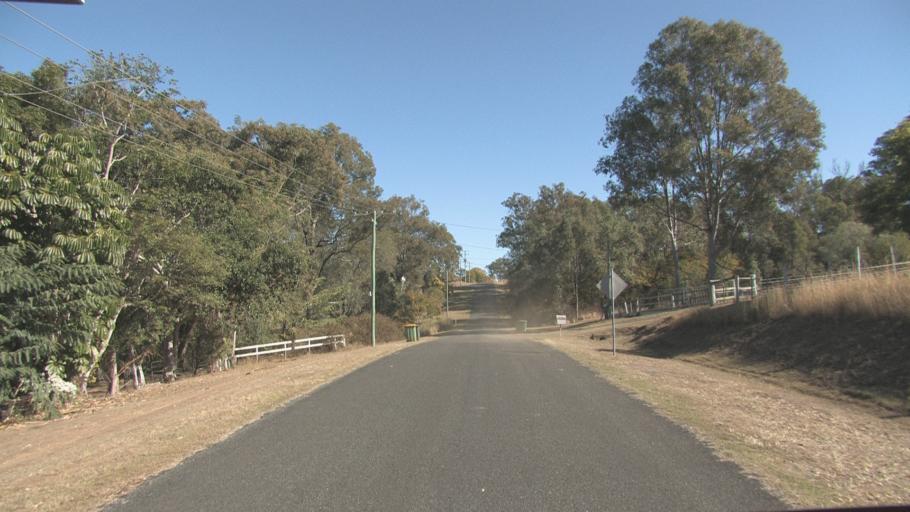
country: AU
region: Queensland
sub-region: Logan
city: Cedar Vale
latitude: -27.8929
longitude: 152.9807
